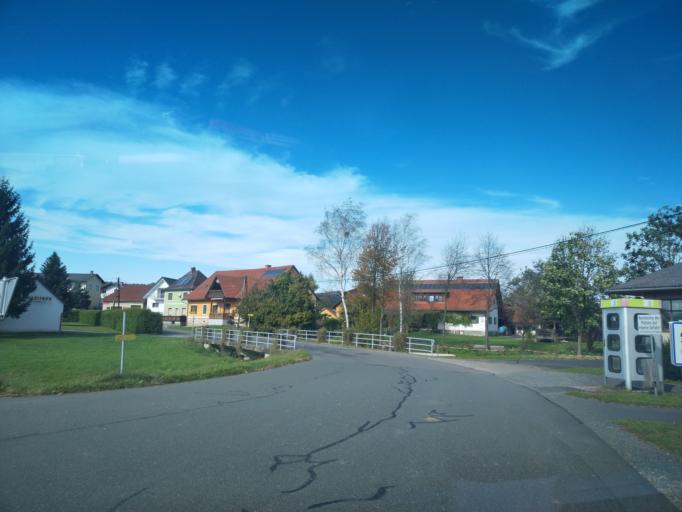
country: AT
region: Styria
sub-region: Politischer Bezirk Leibnitz
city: Sankt Johann im Saggautal
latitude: 46.6990
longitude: 15.3896
